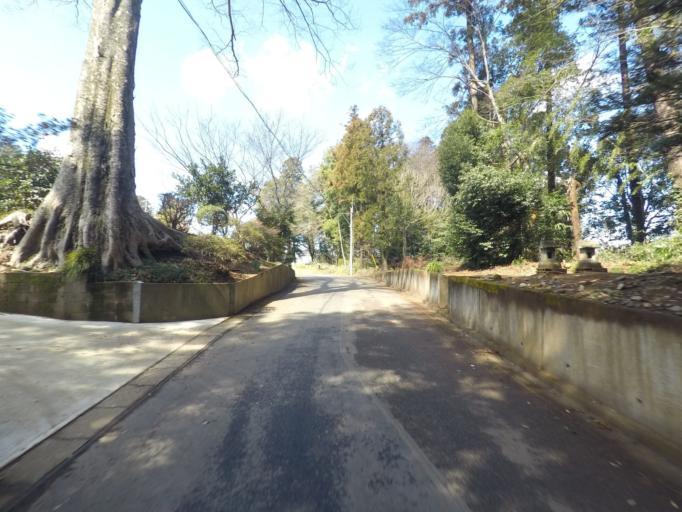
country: JP
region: Ibaraki
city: Ushiku
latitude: 36.0071
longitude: 140.0732
